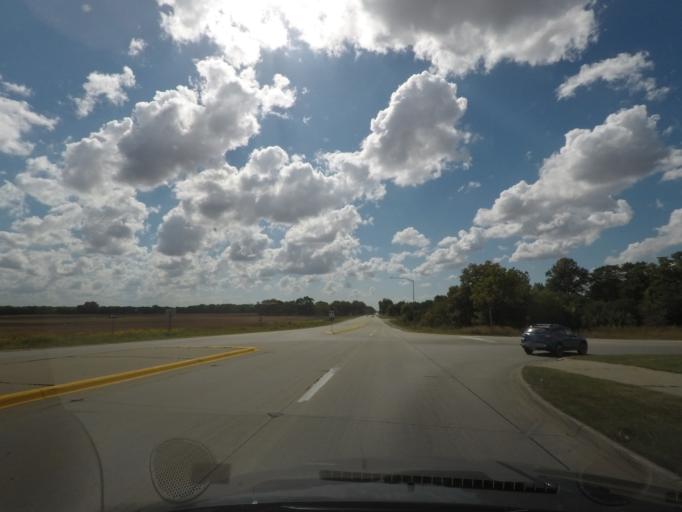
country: US
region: Iowa
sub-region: Story County
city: Ames
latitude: 42.0073
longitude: -93.6788
